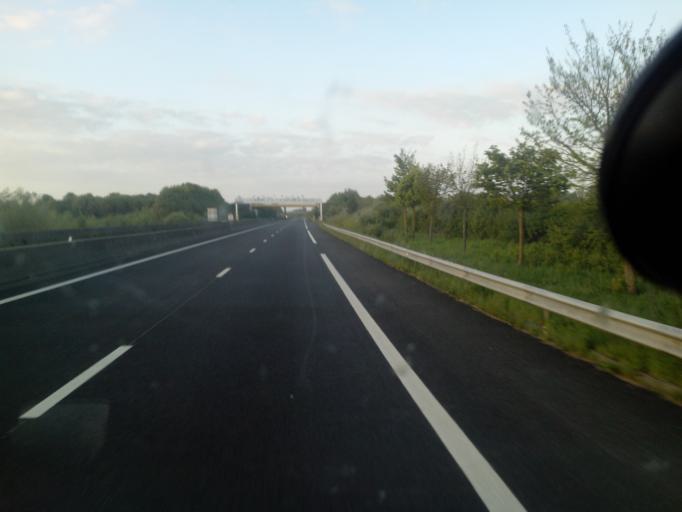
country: FR
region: Picardie
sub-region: Departement de la Somme
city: Bouttencourt
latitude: 49.9667
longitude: 1.6615
